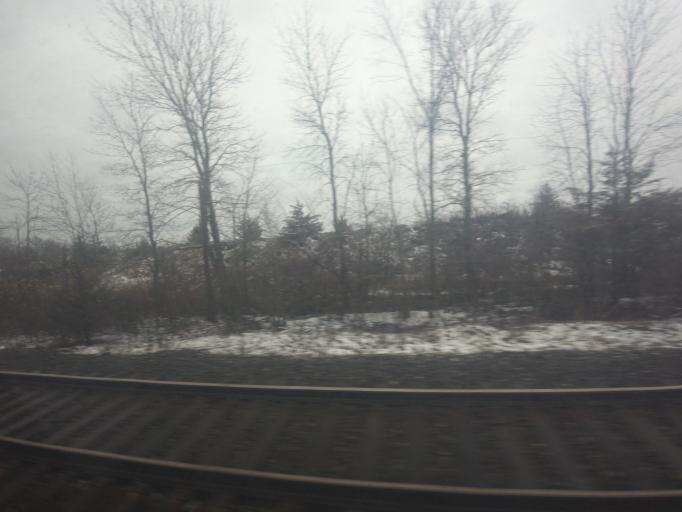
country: CA
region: Ontario
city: Kingston
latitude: 44.2282
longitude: -76.6672
